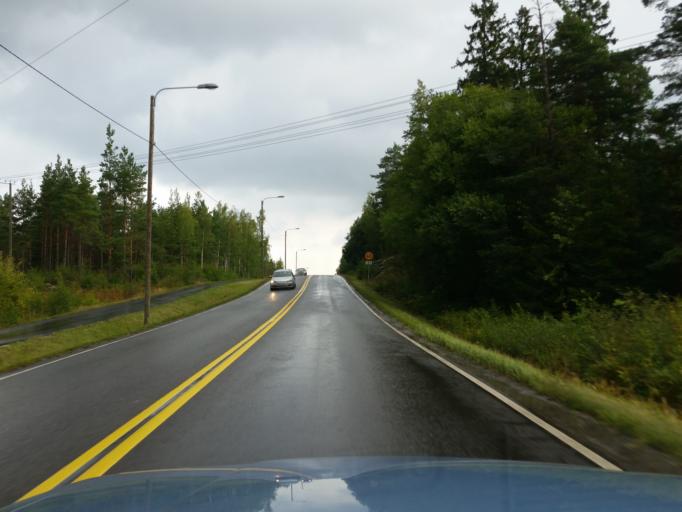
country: FI
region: Varsinais-Suomi
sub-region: Aboland-Turunmaa
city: Laensi-Turunmaa
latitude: 60.2888
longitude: 22.2616
